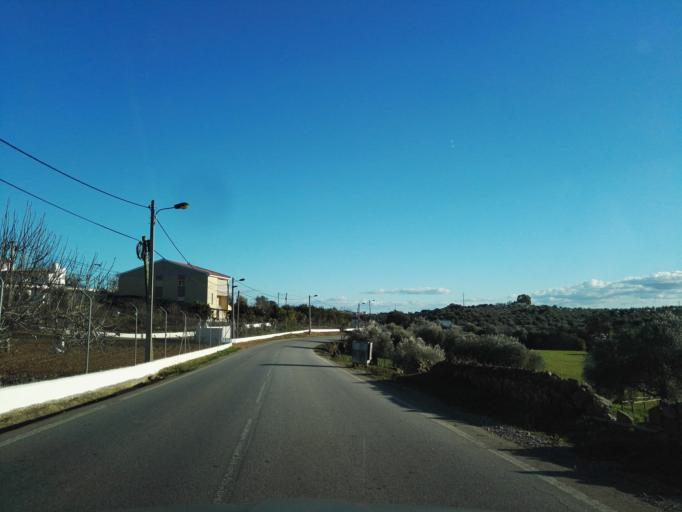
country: PT
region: Portalegre
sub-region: Elvas
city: Elvas
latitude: 38.8996
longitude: -7.1780
